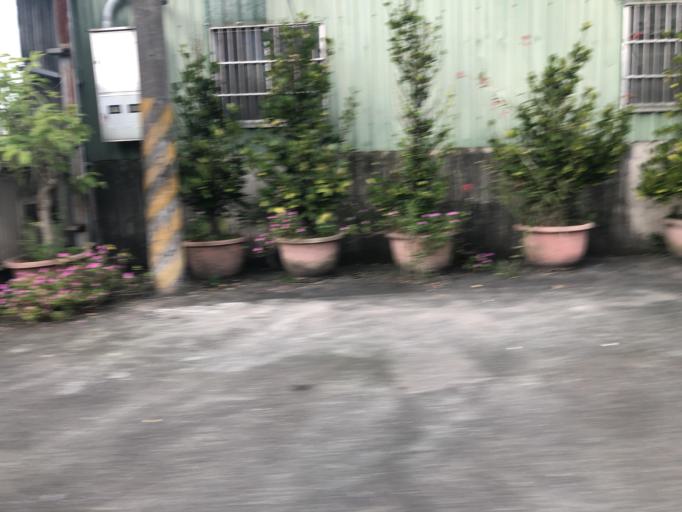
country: TW
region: Taiwan
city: Daxi
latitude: 24.9197
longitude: 121.3638
